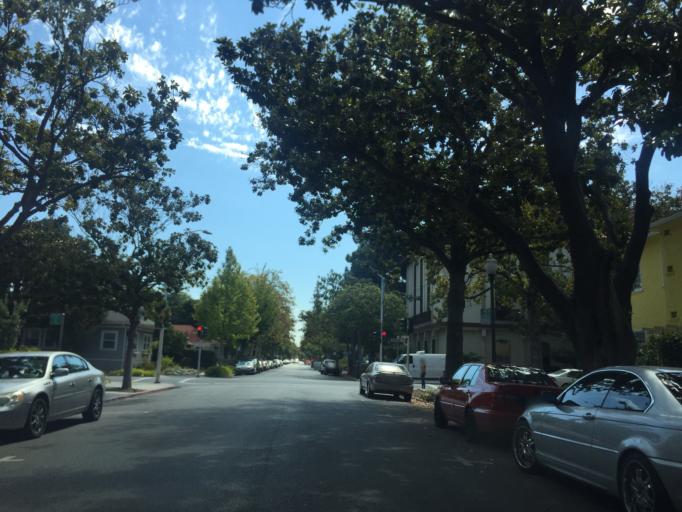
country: US
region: California
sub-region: Santa Clara County
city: Palo Alto
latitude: 37.4490
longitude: -122.1573
